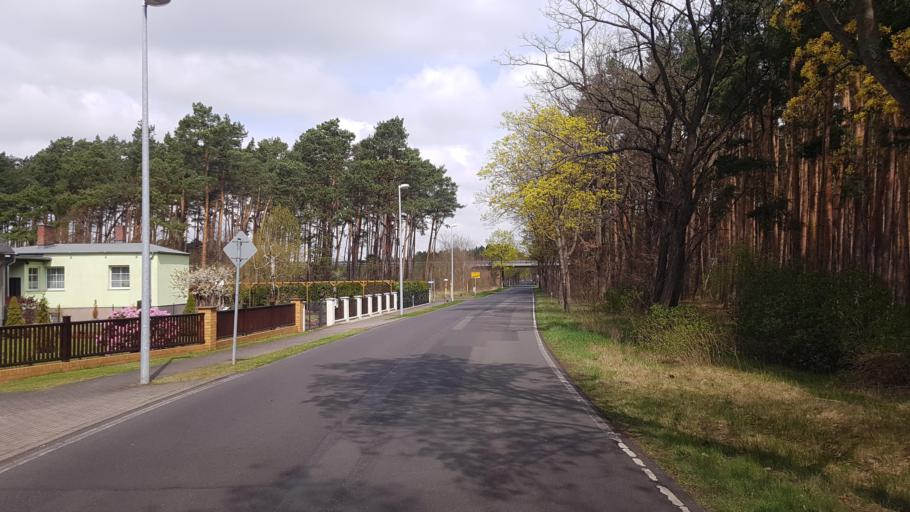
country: DE
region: Brandenburg
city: Luckenwalde
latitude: 52.1234
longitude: 13.1892
